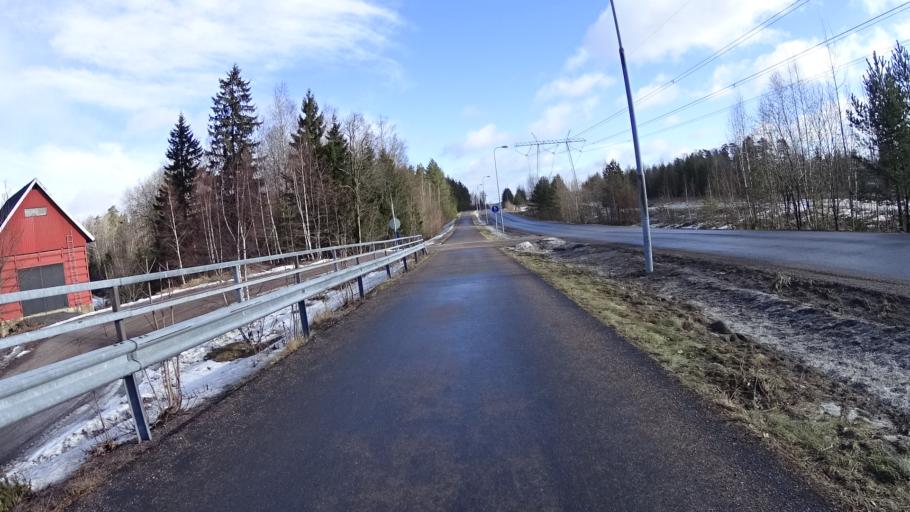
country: FI
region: Uusimaa
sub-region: Helsinki
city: Kauniainen
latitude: 60.2421
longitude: 24.6972
